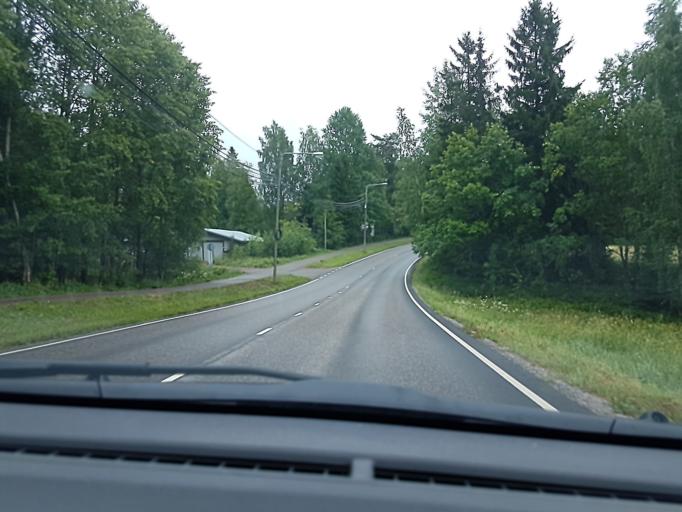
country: FI
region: Uusimaa
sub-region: Helsinki
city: Pornainen
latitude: 60.4730
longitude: 25.3792
